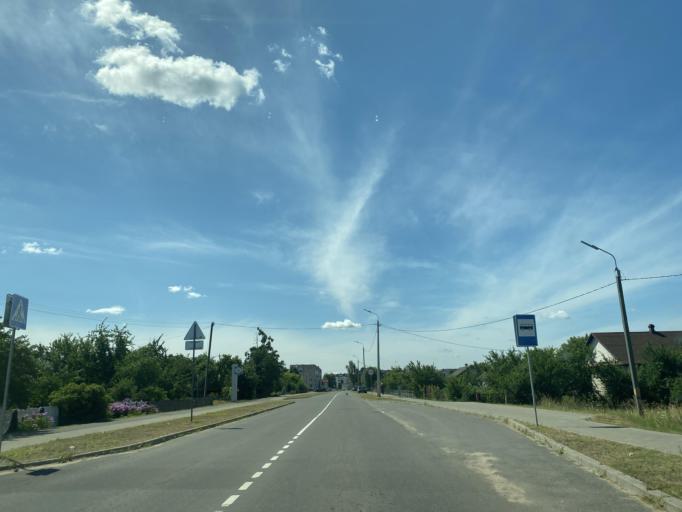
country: BY
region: Brest
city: Ivanava
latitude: 52.1544
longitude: 25.5438
